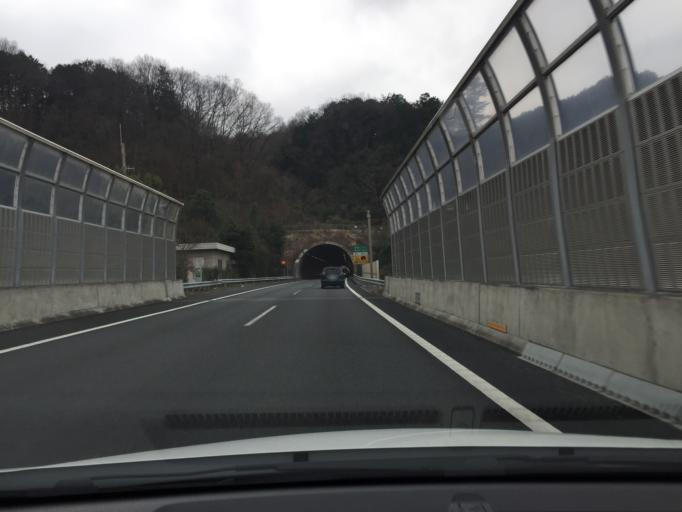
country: JP
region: Tokyo
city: Fussa
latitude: 35.7702
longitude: 139.2898
